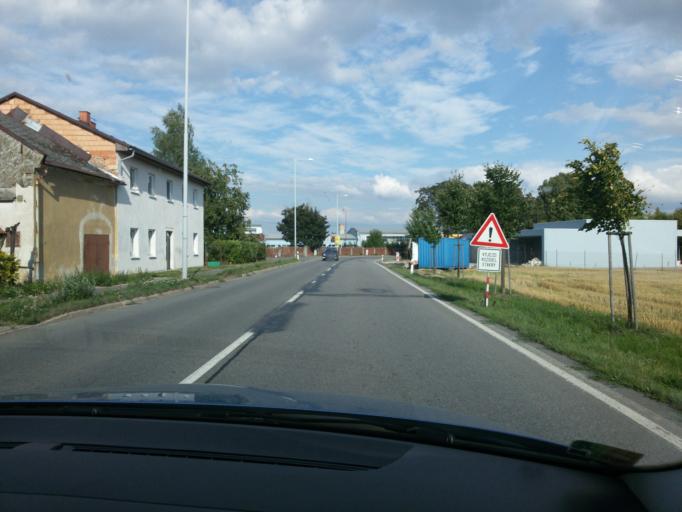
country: CZ
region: Pardubicky
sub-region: Okres Svitavy
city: Policka
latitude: 49.7159
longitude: 16.2526
